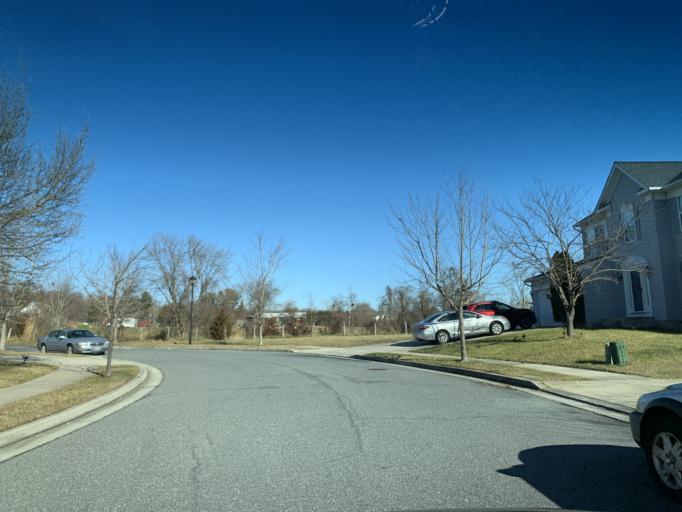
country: US
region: Maryland
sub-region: Baltimore County
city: Perry Hall
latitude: 39.4070
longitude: -76.4599
